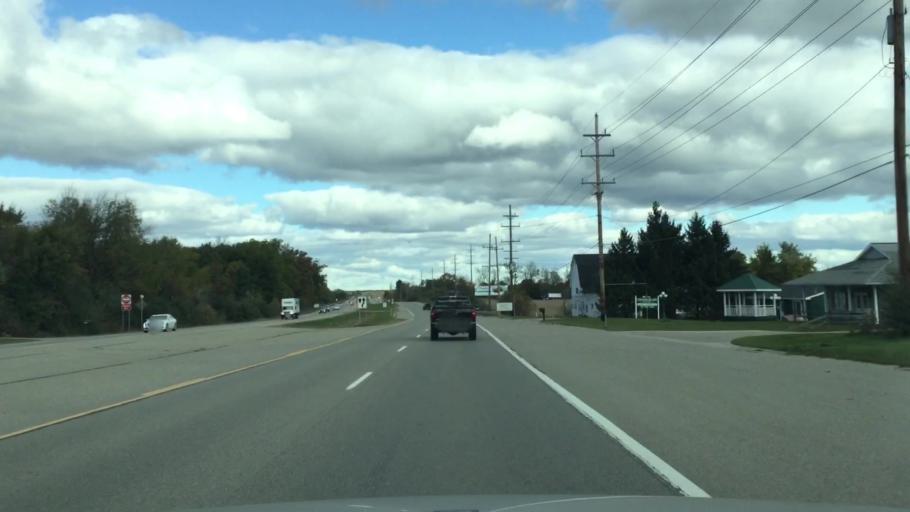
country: US
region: Michigan
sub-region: Lapeer County
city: Lapeer
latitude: 42.9589
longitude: -83.3139
